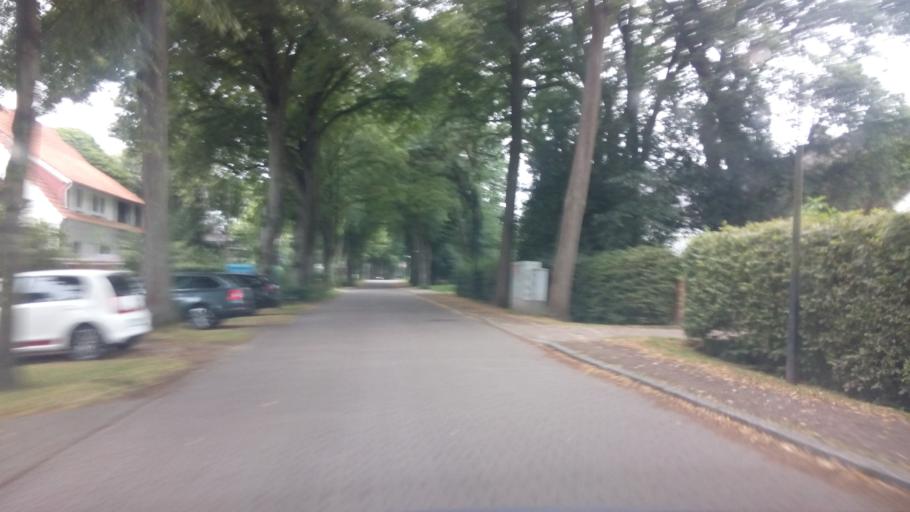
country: DE
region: Lower Saxony
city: Lilienthal
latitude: 53.1208
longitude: 8.8857
